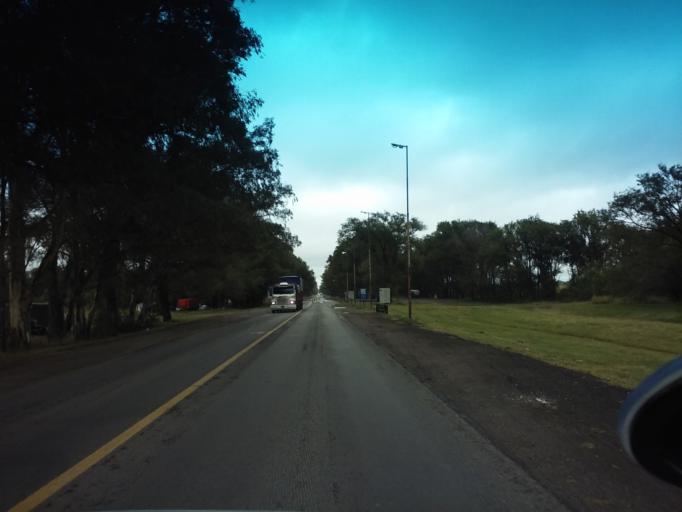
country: AR
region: La Pampa
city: Catrilo
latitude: -36.4104
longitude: -63.3844
